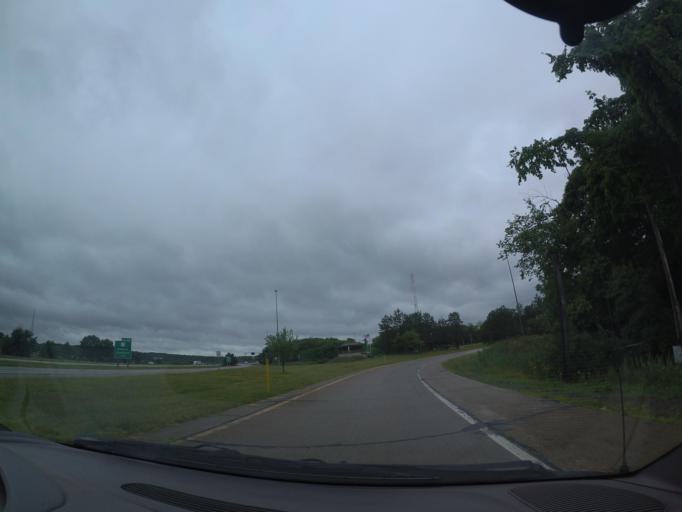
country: US
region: Ohio
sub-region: Ashtabula County
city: Conneaut
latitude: 41.9248
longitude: -80.5460
